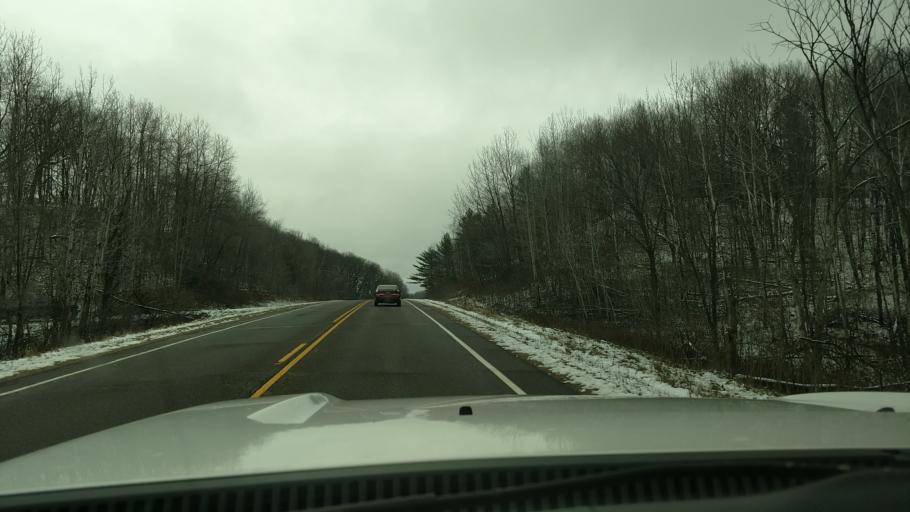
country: US
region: Wisconsin
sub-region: Dunn County
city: Boyceville
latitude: 45.1362
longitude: -91.9868
